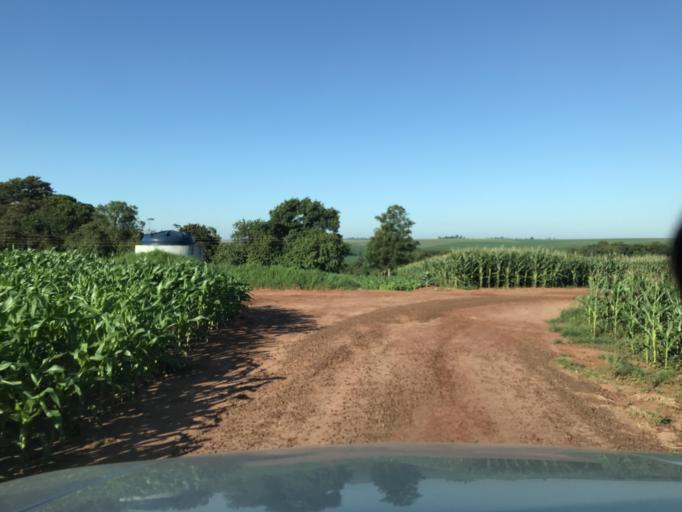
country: BR
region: Parana
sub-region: Palotina
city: Palotina
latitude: -24.2350
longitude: -53.7647
